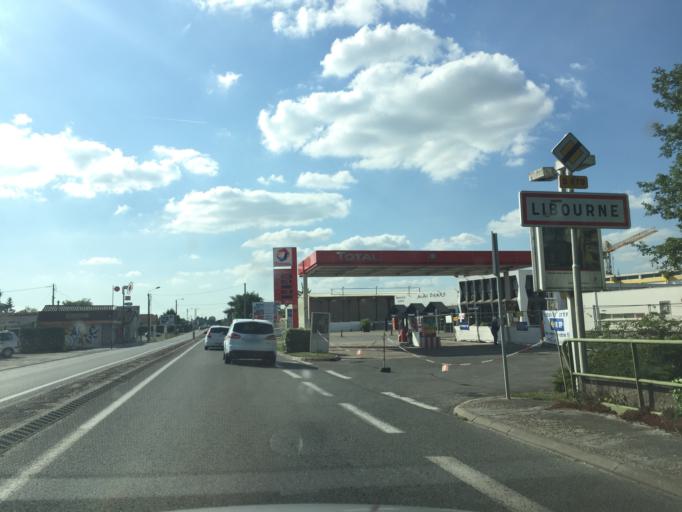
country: FR
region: Aquitaine
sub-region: Departement de la Gironde
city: Libourne
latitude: 44.8974
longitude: -0.2084
